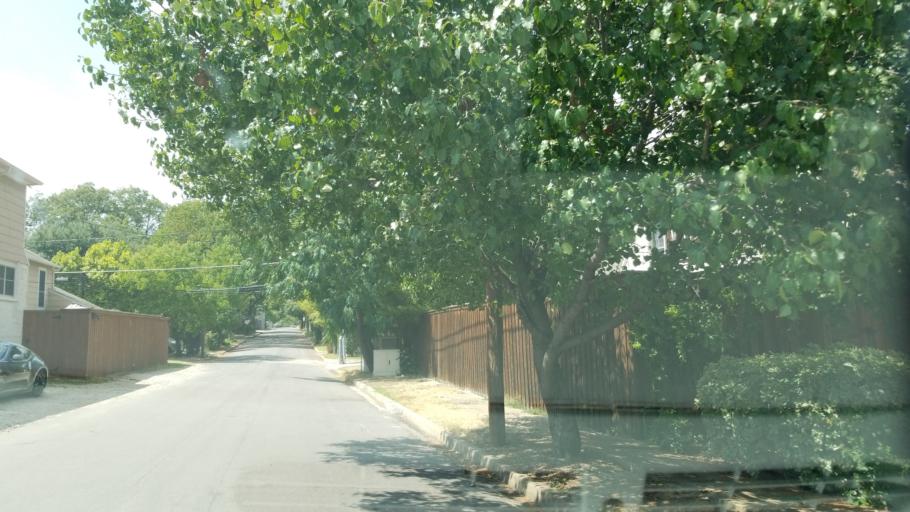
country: US
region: Texas
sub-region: Dallas County
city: Dallas
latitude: 32.7554
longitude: -96.8403
